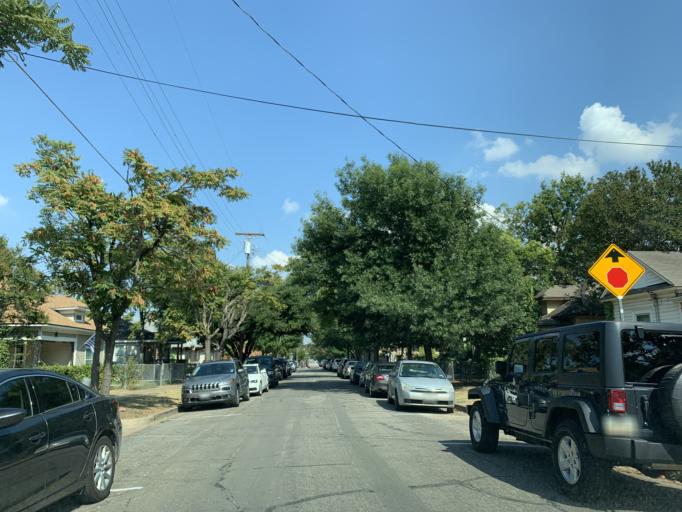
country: US
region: Texas
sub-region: Dallas County
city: Dallas
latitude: 32.7481
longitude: -96.8297
